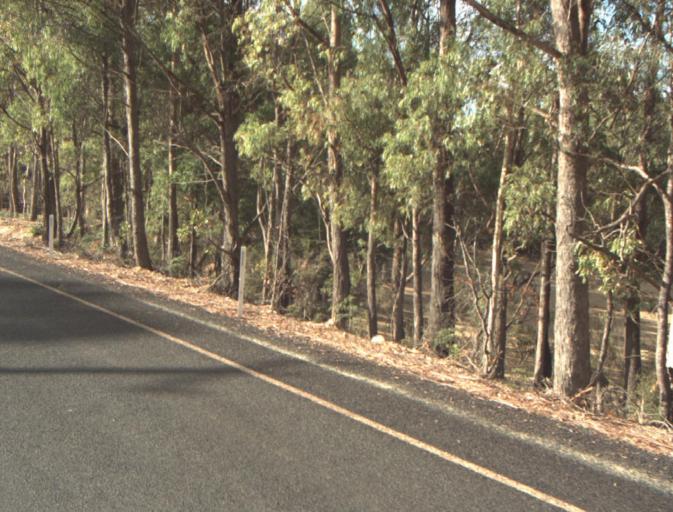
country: AU
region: Tasmania
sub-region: Dorset
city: Bridport
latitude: -41.1660
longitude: 147.2521
